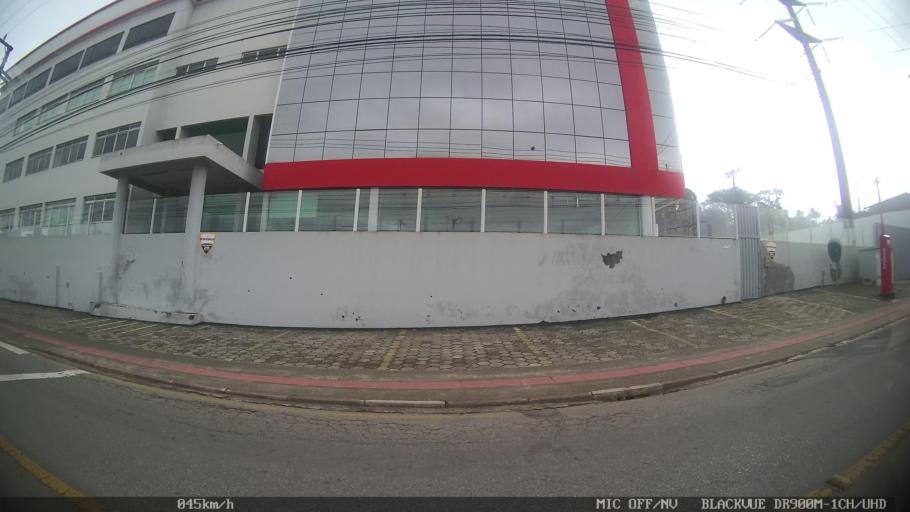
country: BR
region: Santa Catarina
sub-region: Sao Jose
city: Campinas
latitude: -27.5866
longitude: -48.6200
